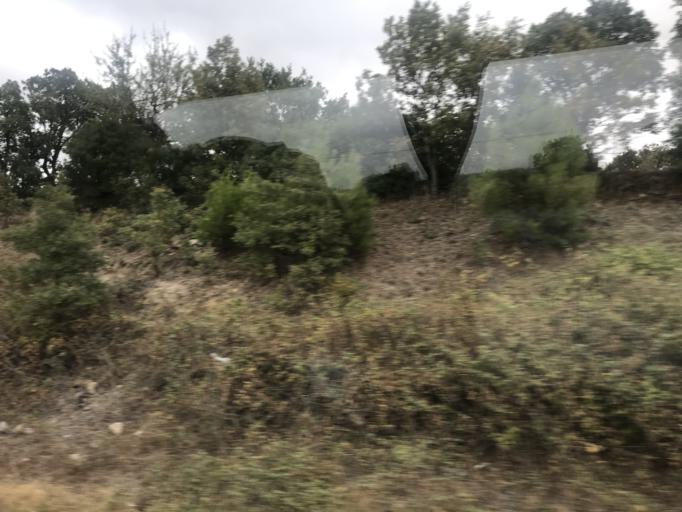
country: TR
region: Balikesir
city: Ivrindi
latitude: 39.6341
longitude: 27.4260
